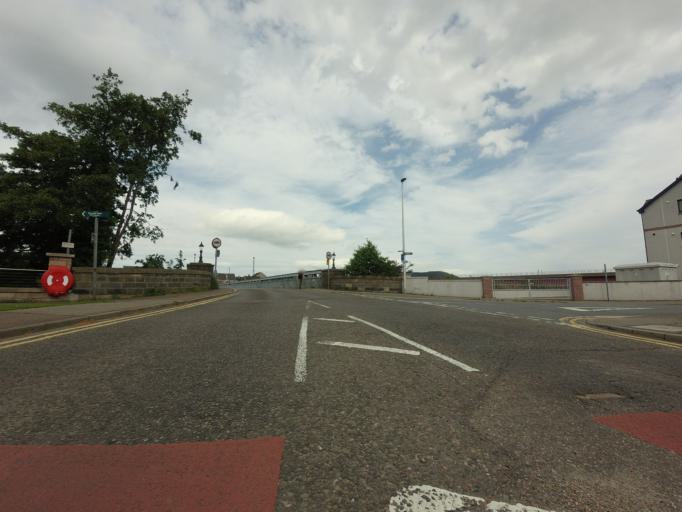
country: GB
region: Scotland
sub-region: Highland
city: Inverness
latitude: 57.4832
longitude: -4.2316
